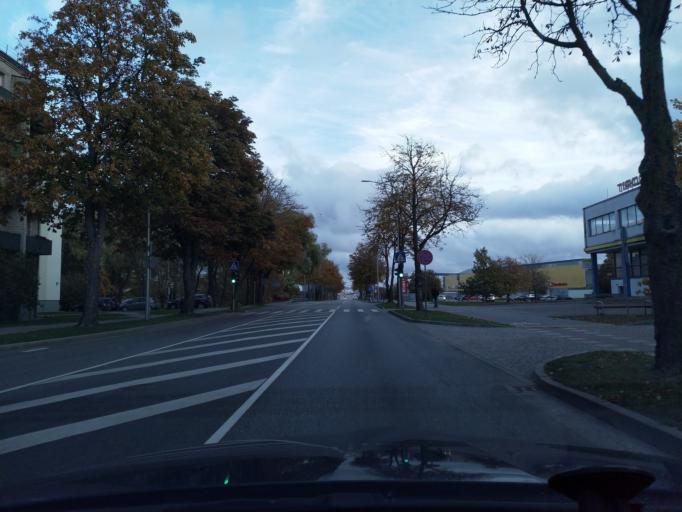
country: LV
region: Ventspils
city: Ventspils
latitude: 57.3890
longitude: 21.5771
